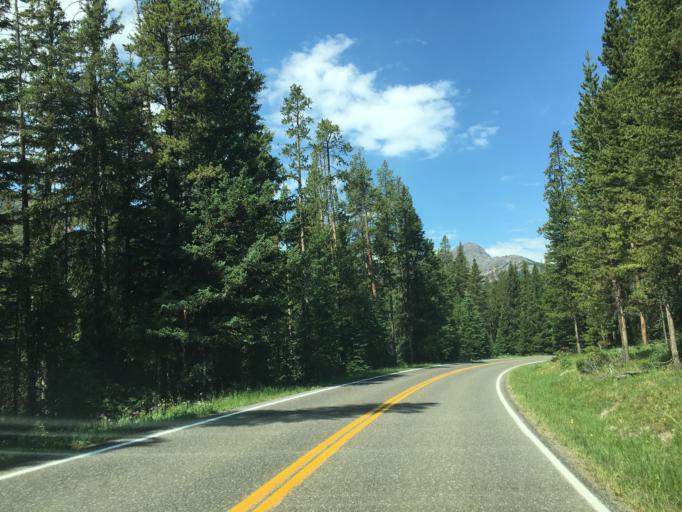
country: US
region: Montana
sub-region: Stillwater County
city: Absarokee
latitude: 45.0038
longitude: -110.0128
